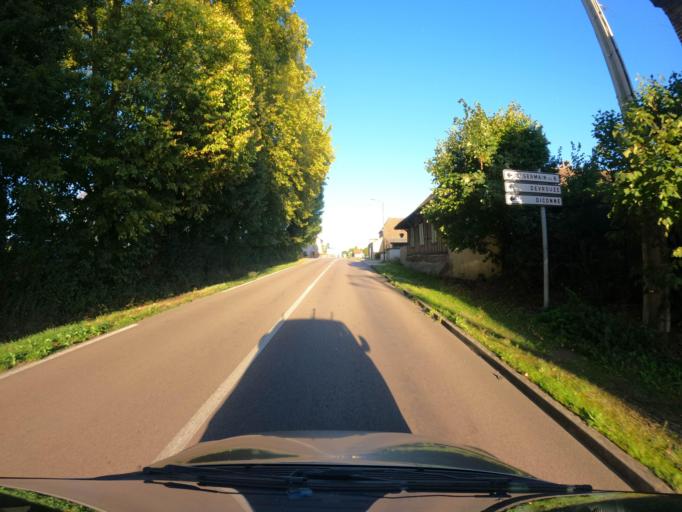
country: FR
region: Bourgogne
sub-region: Departement de Saone-et-Loire
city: Mervans
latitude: 46.7432
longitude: 5.1198
